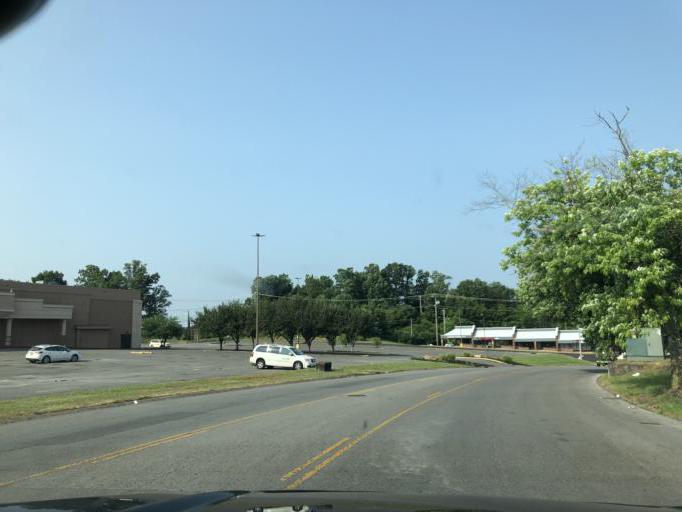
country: US
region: Tennessee
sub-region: Rutherford County
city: La Vergne
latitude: 36.0478
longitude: -86.6466
